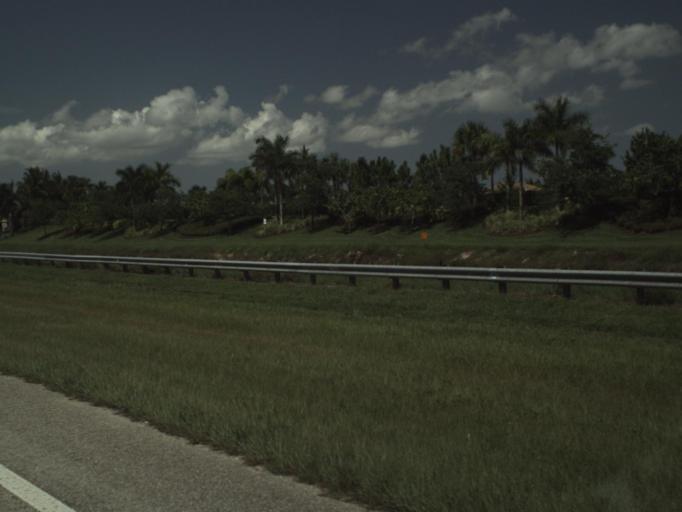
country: US
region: Florida
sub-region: Palm Beach County
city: Villages of Oriole
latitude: 26.5140
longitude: -80.2051
